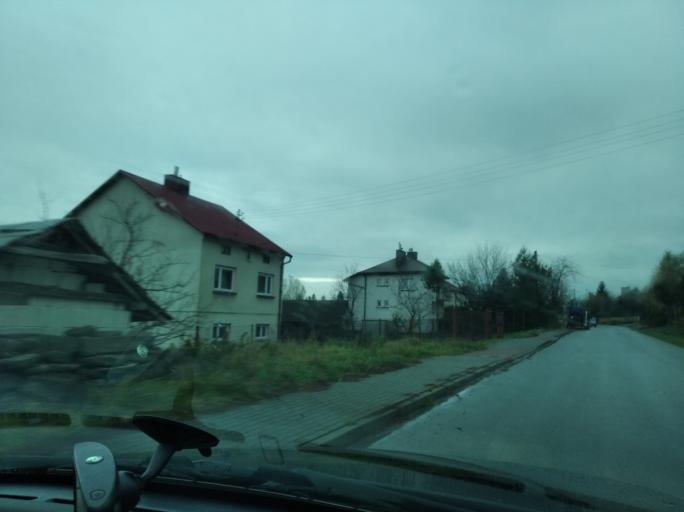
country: PL
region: Subcarpathian Voivodeship
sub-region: Powiat rzeszowski
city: Tyczyn
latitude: 49.9585
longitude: 22.0454
